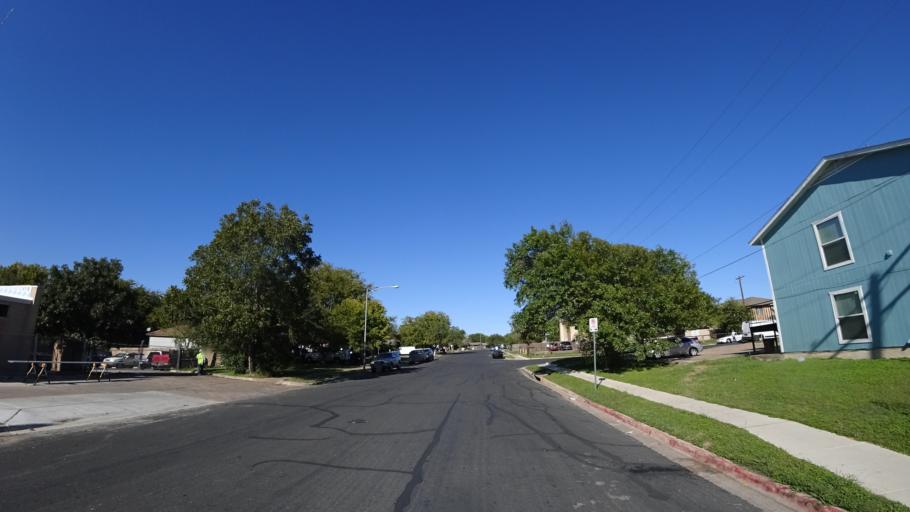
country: US
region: Texas
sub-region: Travis County
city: Hornsby Bend
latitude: 30.2933
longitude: -97.6313
